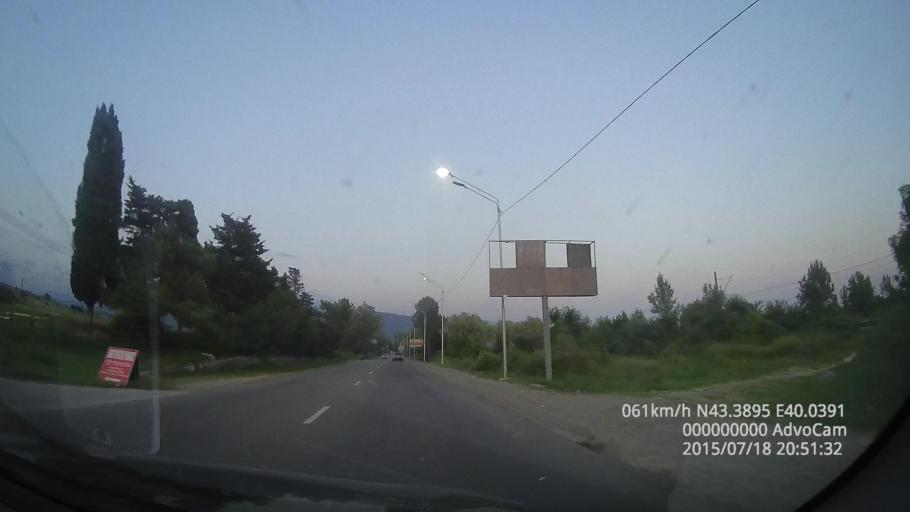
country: GE
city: Gantiadi
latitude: 43.3892
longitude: 40.0408
